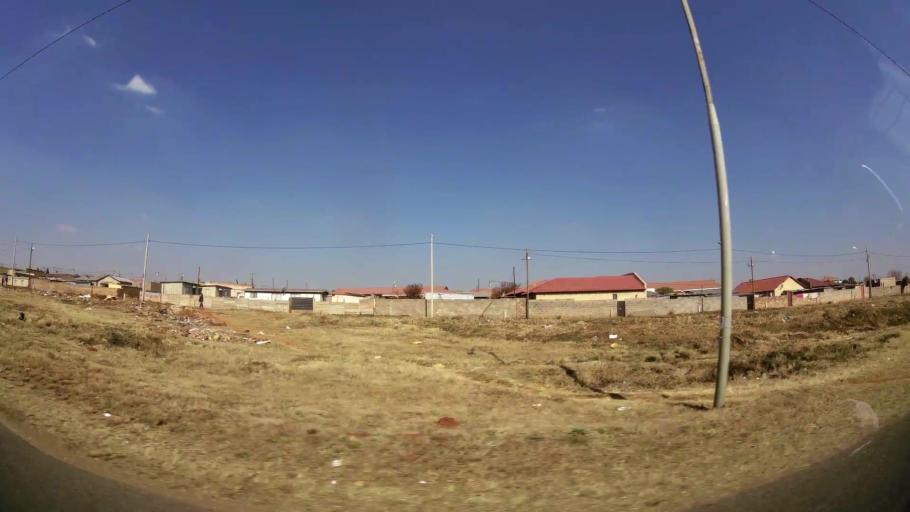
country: ZA
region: Gauteng
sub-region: West Rand District Municipality
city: Randfontein
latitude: -26.1722
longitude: 27.7832
